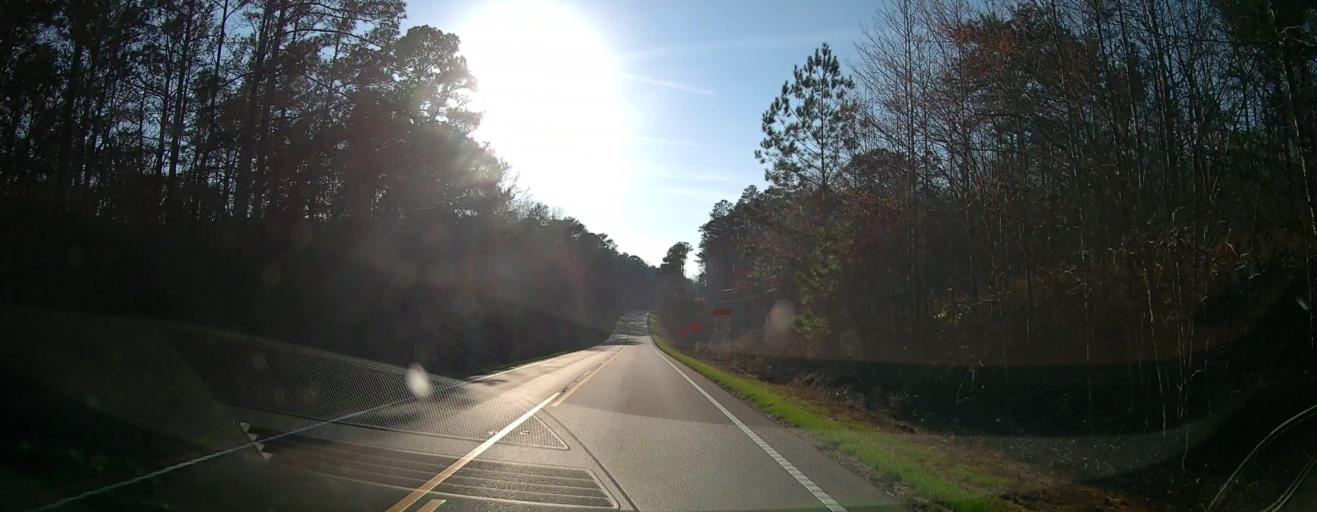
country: US
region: Georgia
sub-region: Harris County
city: Hamilton
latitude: 32.7409
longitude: -84.9554
